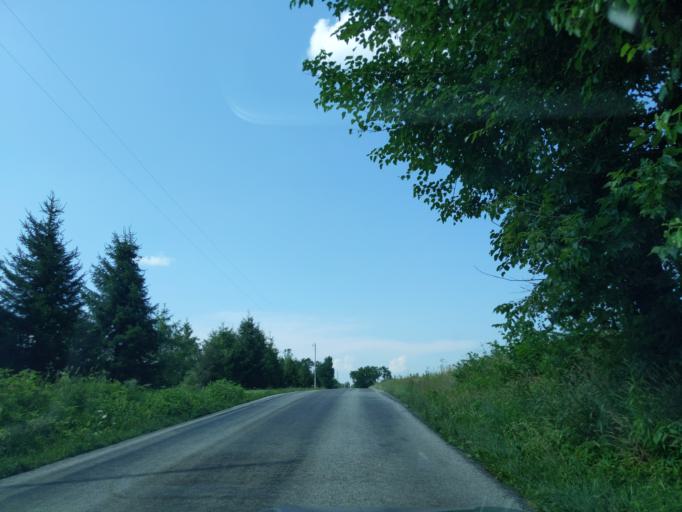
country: US
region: Indiana
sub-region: Ripley County
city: Osgood
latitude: 39.1010
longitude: -85.3450
